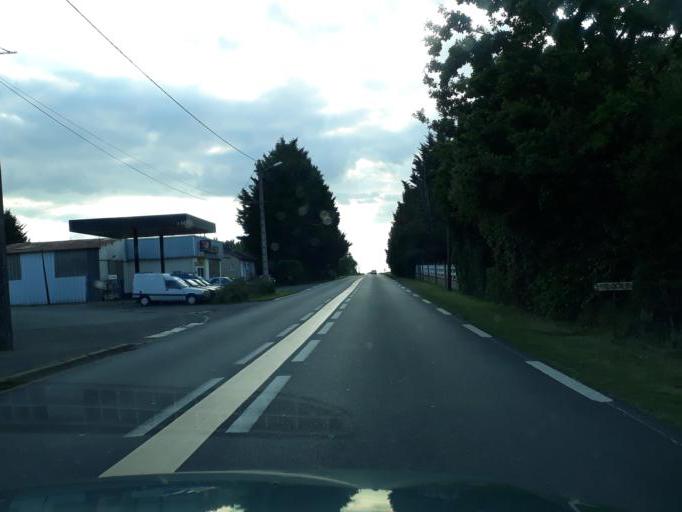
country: FR
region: Centre
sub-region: Departement du Loir-et-Cher
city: Aze
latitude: 47.8934
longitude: 1.0226
